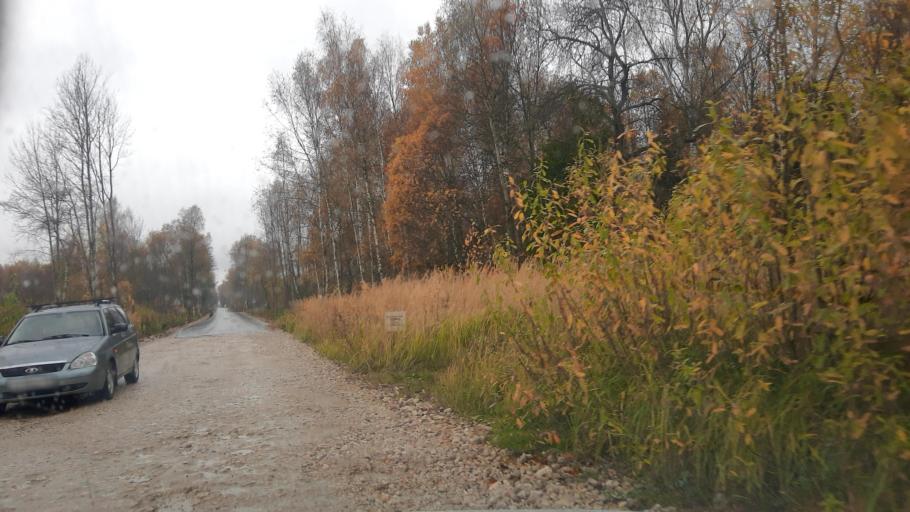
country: RU
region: Moskovskaya
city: Elektrostal'
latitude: 55.7991
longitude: 38.3736
